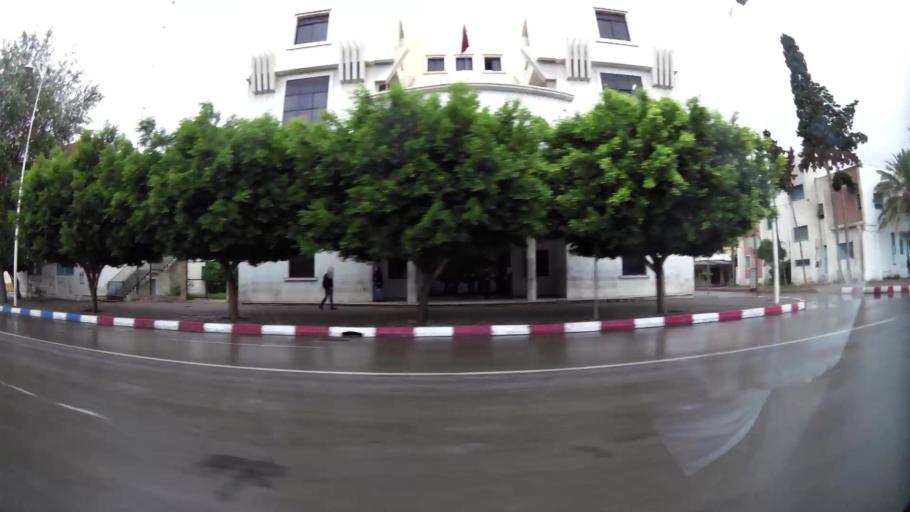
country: MA
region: Oriental
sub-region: Nador
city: Nador
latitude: 35.1740
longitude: -2.9250
